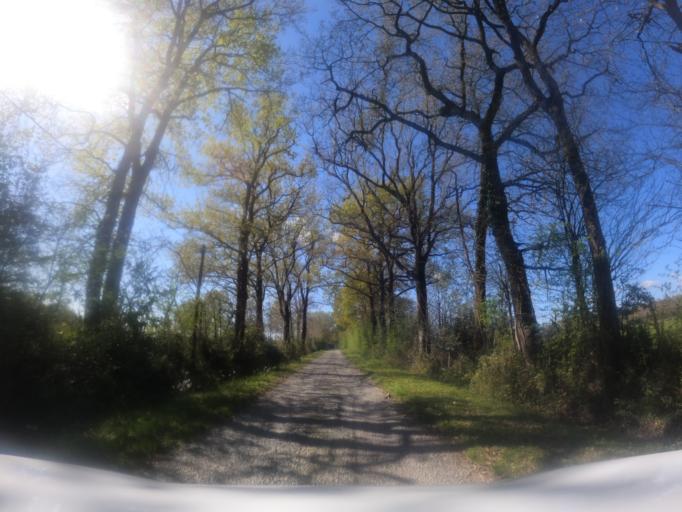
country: FR
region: Pays de la Loire
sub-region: Departement de la Vendee
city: Saint-Vincent-sur-Graon
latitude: 46.5212
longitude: -1.3668
